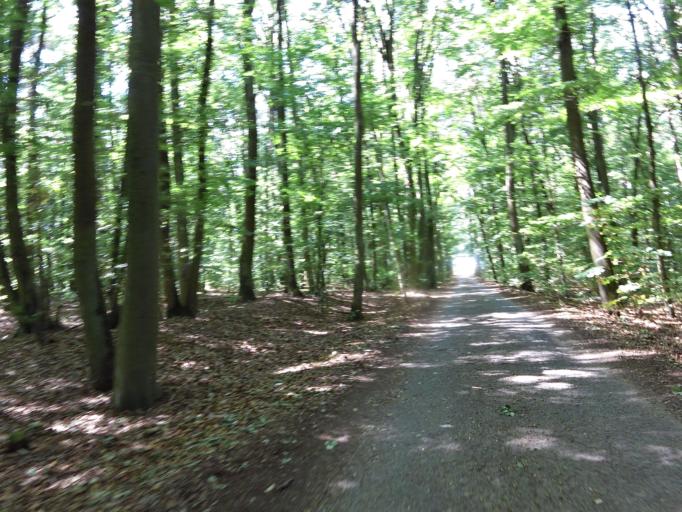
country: DE
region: Bavaria
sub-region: Regierungsbezirk Unterfranken
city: Theilheim
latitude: 49.7489
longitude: 10.0179
